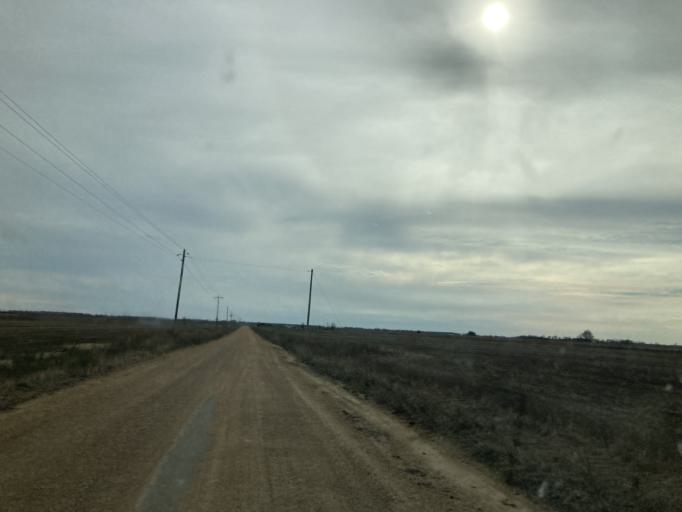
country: US
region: Mississippi
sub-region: Humphreys County
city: Belzoni
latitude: 33.1828
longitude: -90.5722
